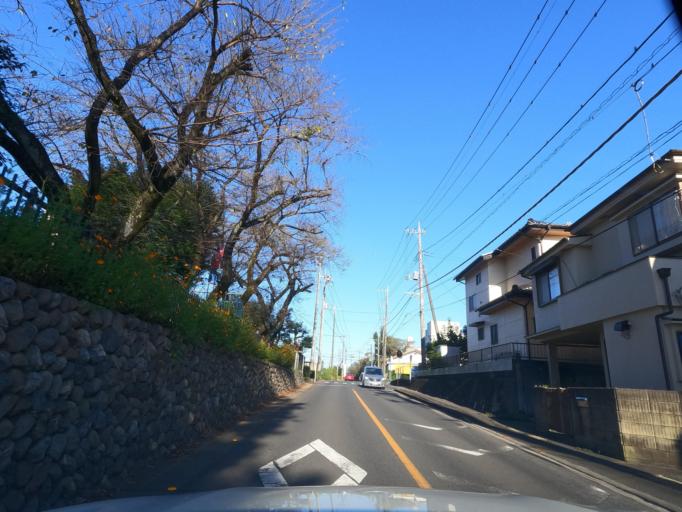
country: JP
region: Saitama
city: Hanno
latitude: 35.8661
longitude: 139.3413
